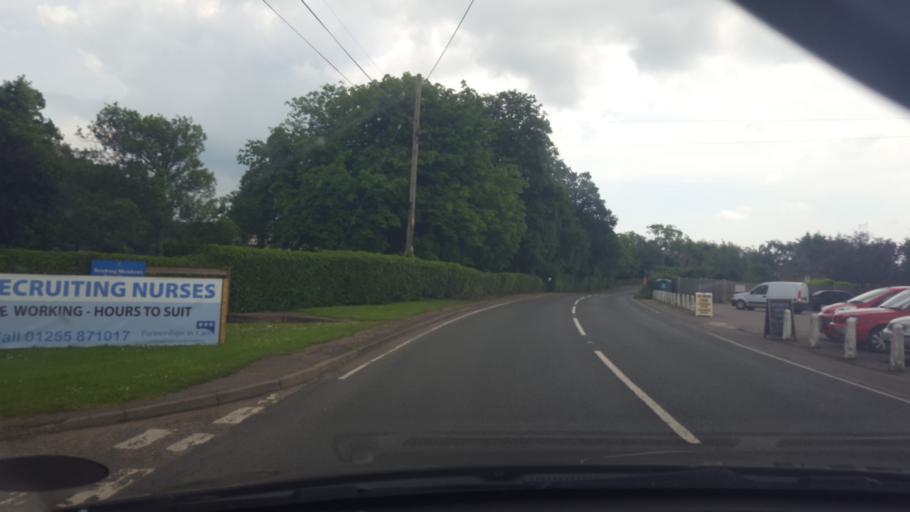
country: GB
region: England
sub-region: Essex
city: Mistley
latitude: 51.8954
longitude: 1.0988
